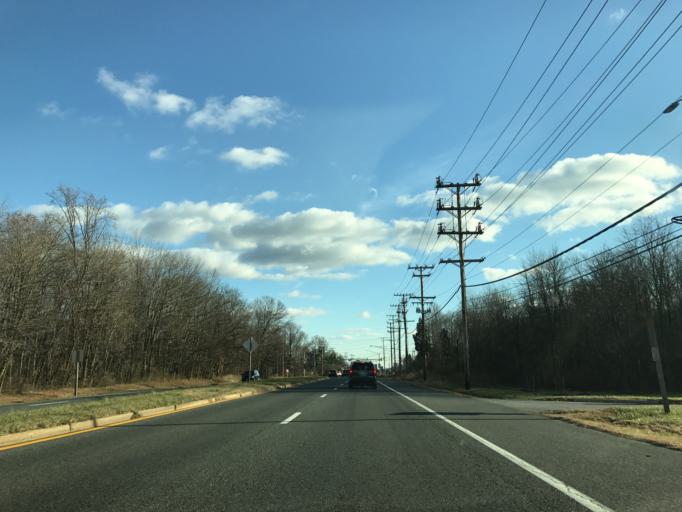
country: US
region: Maryland
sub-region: Harford County
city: Fallston
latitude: 39.5002
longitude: -76.3990
